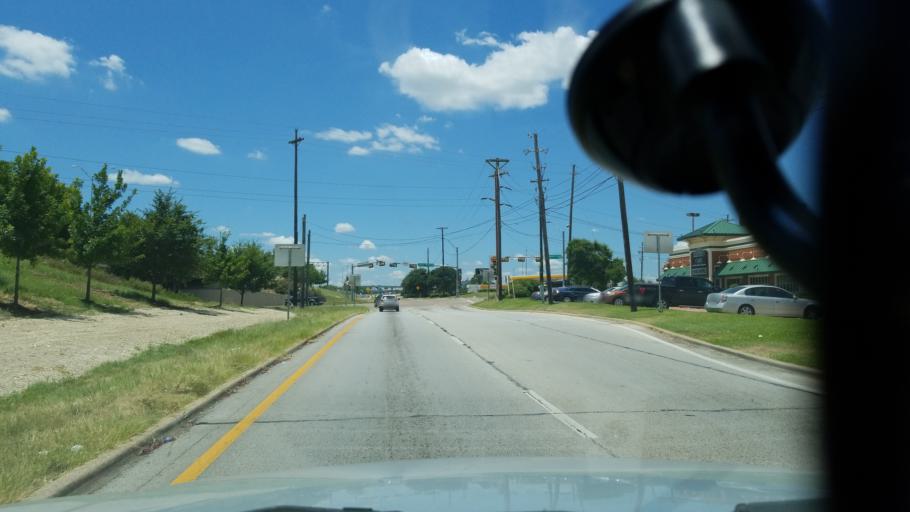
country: US
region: Texas
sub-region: Dallas County
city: Duncanville
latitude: 32.6629
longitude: -96.8699
